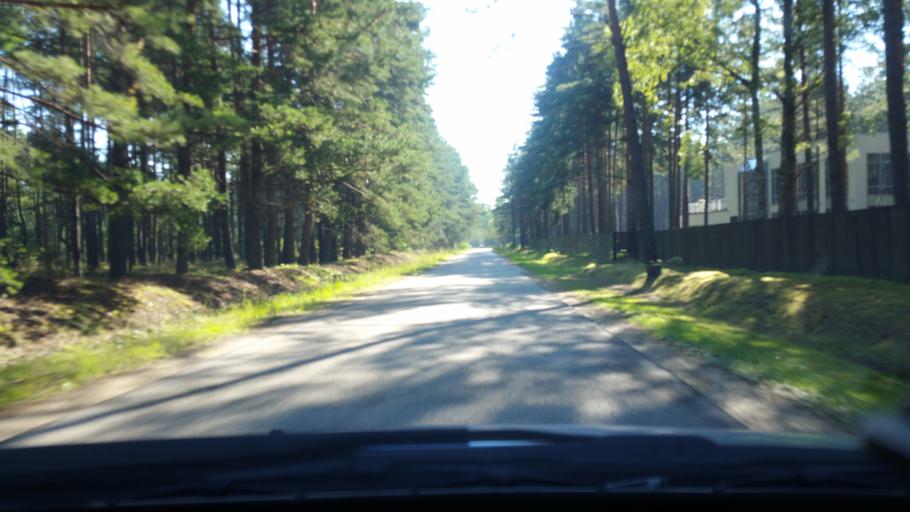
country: LV
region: Adazi
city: Adazi
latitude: 57.1239
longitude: 24.3410
